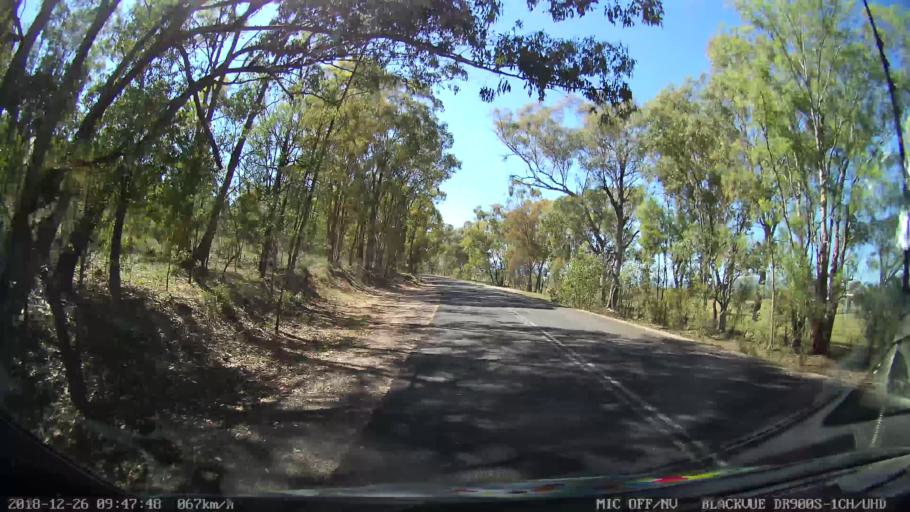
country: AU
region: New South Wales
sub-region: Mid-Western Regional
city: Kandos
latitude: -32.9826
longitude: 150.1084
